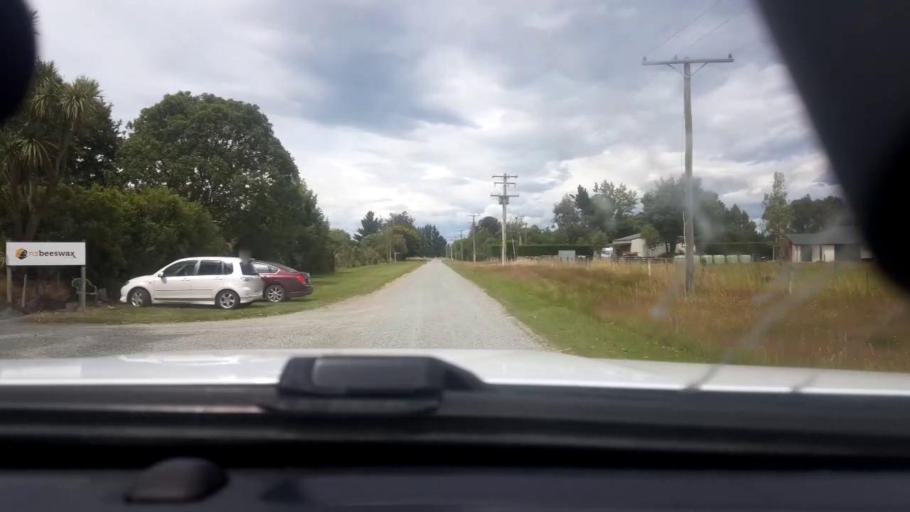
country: NZ
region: Canterbury
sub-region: Timaru District
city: Pleasant Point
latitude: -44.1409
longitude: 171.2903
